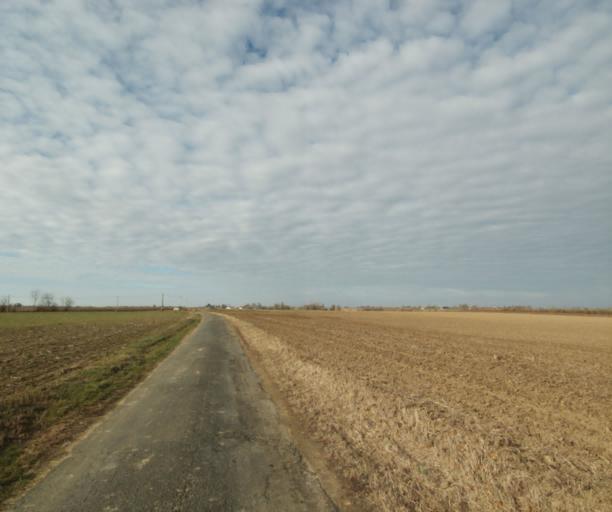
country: FR
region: Poitou-Charentes
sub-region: Departement de la Charente-Maritime
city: Corme-Royal
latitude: 45.7293
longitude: -0.7908
